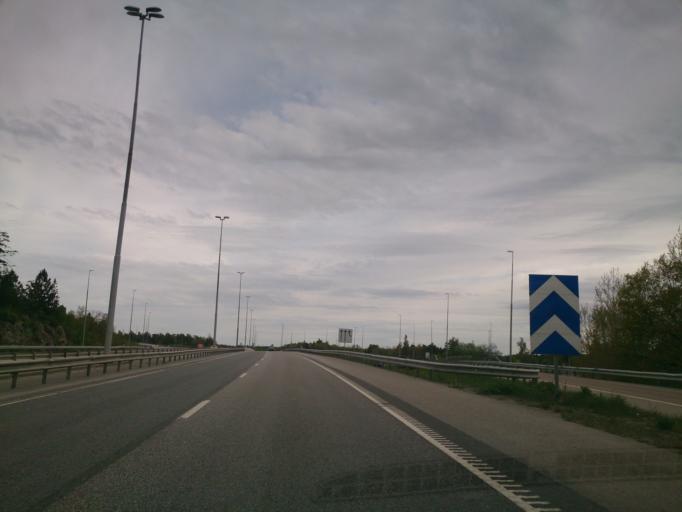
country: SE
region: Stockholm
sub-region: Haninge Kommun
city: Handen
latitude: 59.2324
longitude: 18.1235
